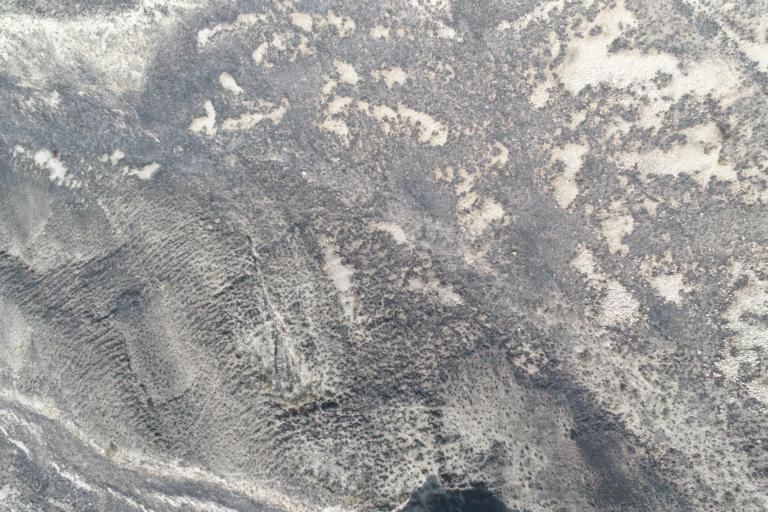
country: BO
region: La Paz
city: La Paz
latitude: -16.4704
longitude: -68.0970
